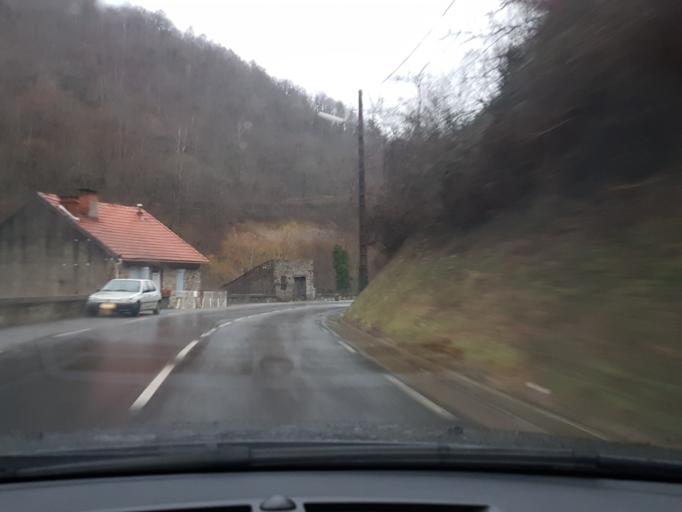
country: FR
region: Midi-Pyrenees
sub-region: Departement de l'Ariege
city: Saint-Girons
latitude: 42.9414
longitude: 1.1764
